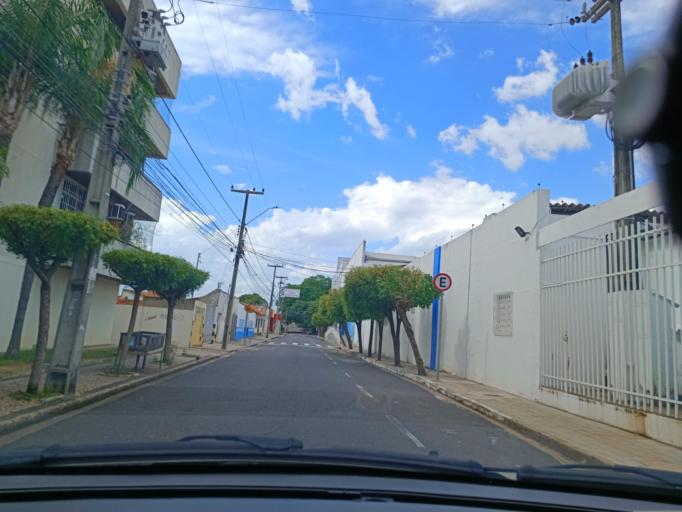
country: BR
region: Piaui
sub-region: Teresina
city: Teresina
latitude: -5.0849
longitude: -42.8143
